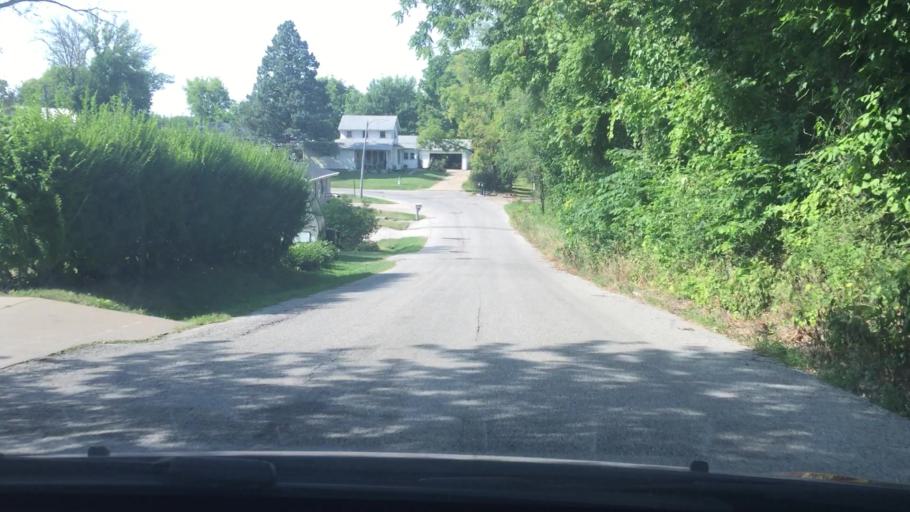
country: US
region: Iowa
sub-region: Muscatine County
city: Muscatine
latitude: 41.4311
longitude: -91.0614
